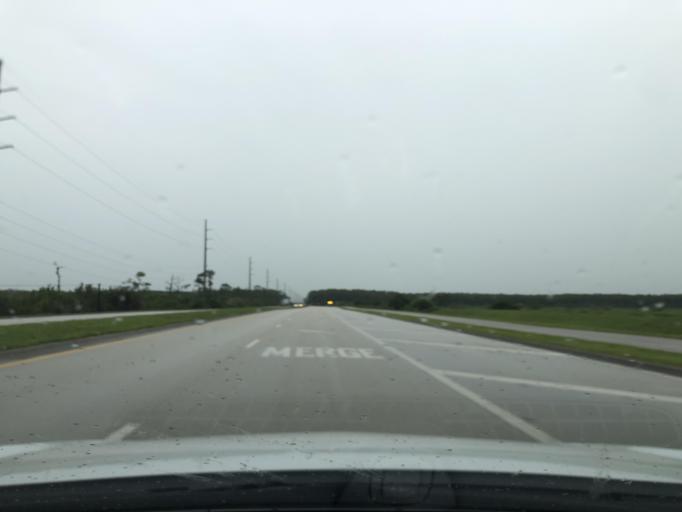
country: US
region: Florida
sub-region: Collier County
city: Orangetree
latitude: 26.2941
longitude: -81.4835
